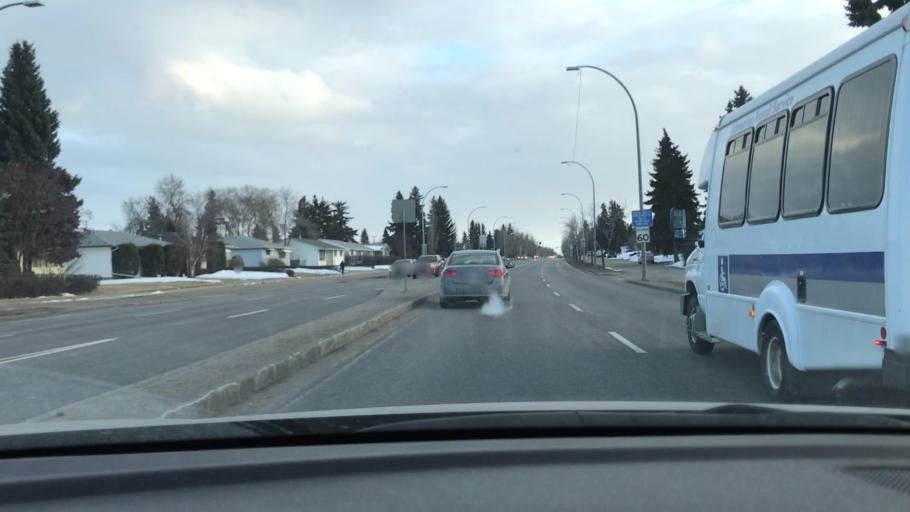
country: CA
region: Alberta
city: Edmonton
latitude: 53.5371
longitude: -113.4430
